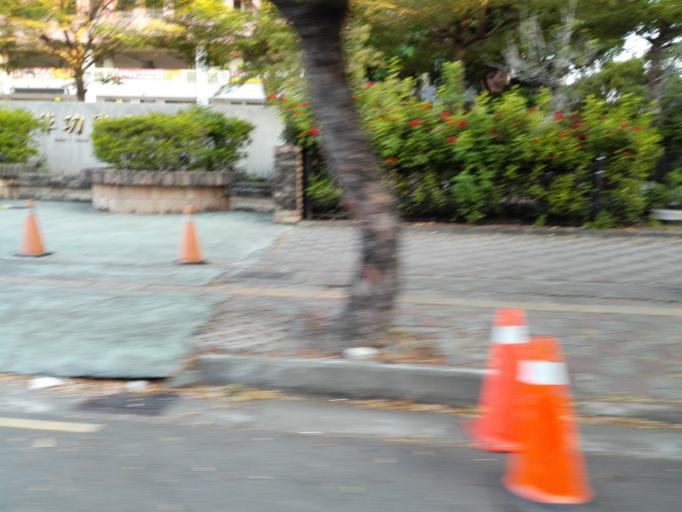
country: TW
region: Taiwan
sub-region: Taichung City
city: Taichung
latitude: 24.1726
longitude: 120.7197
